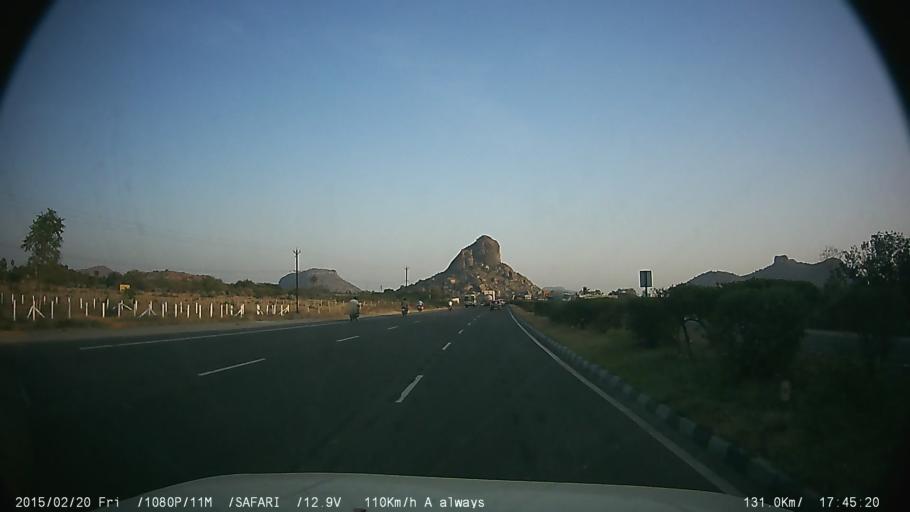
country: IN
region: Tamil Nadu
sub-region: Krishnagiri
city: Krishnagiri
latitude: 12.5574
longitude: 78.1856
